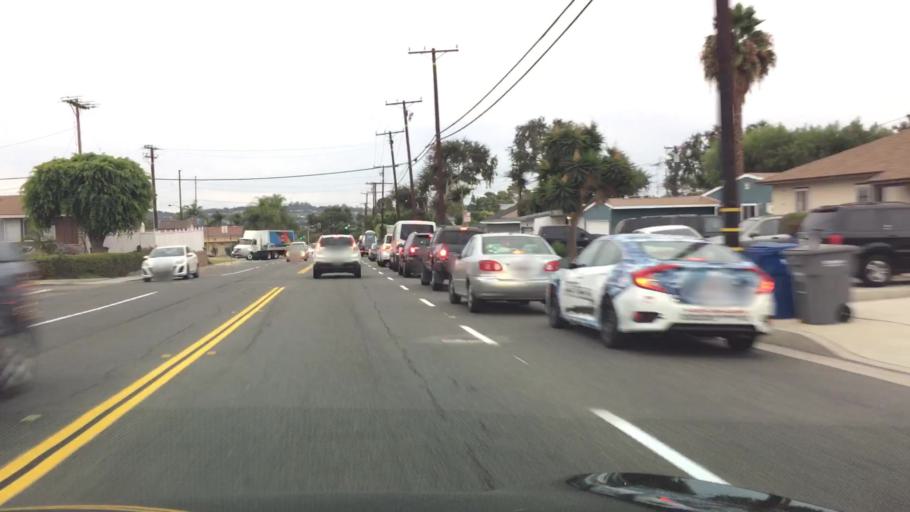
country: US
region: California
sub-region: Orange County
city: La Habra
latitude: 33.9418
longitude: -117.9648
